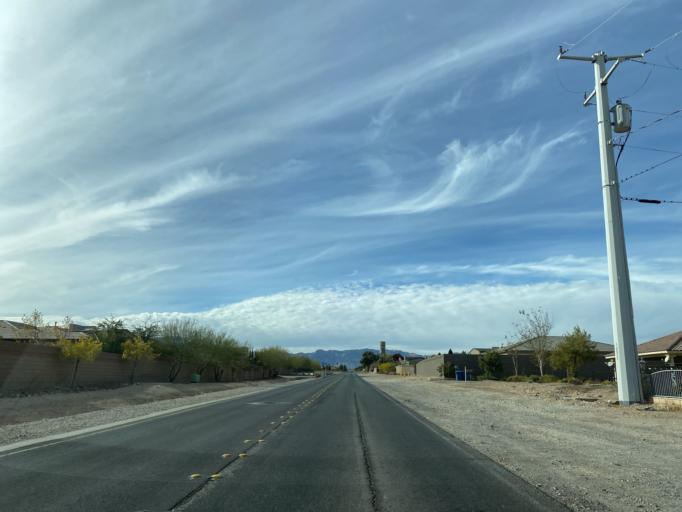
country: US
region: Nevada
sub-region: Clark County
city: Enterprise
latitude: 36.0337
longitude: -115.2639
